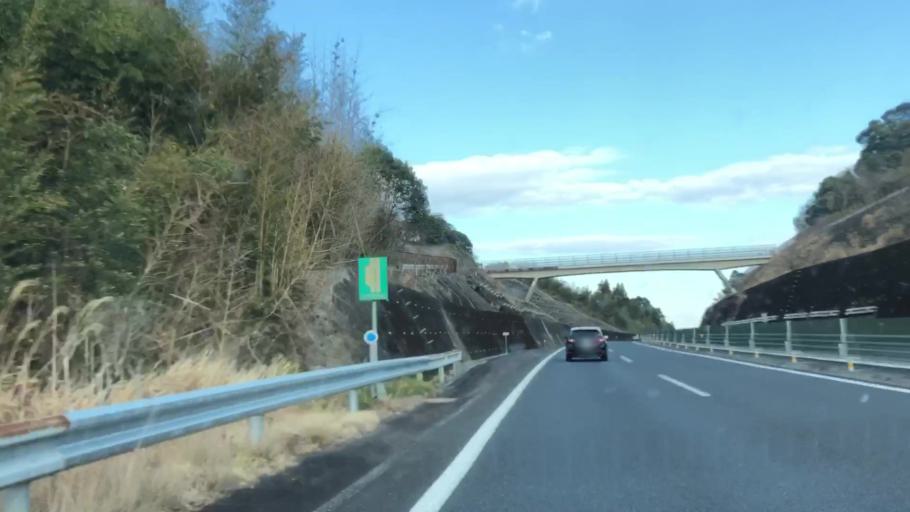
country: JP
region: Miyazaki
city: Miyazaki-shi
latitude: 31.8642
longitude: 131.3834
